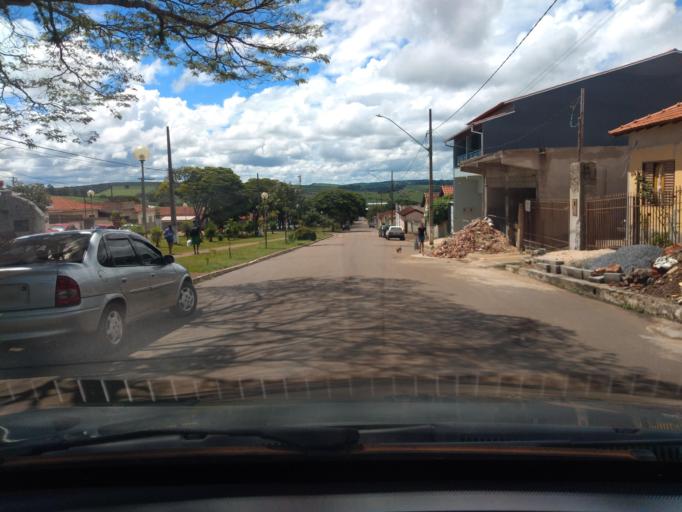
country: BR
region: Minas Gerais
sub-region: Tres Coracoes
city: Tres Coracoes
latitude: -21.5880
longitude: -45.0689
